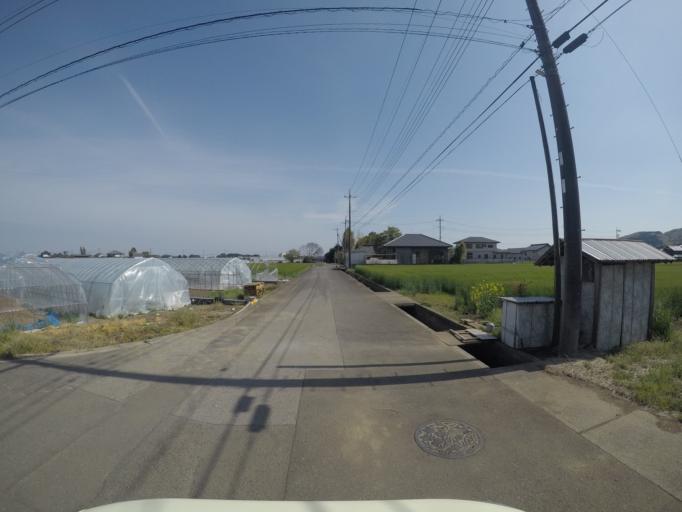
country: JP
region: Tochigi
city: Tochigi
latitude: 36.4451
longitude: 139.7208
